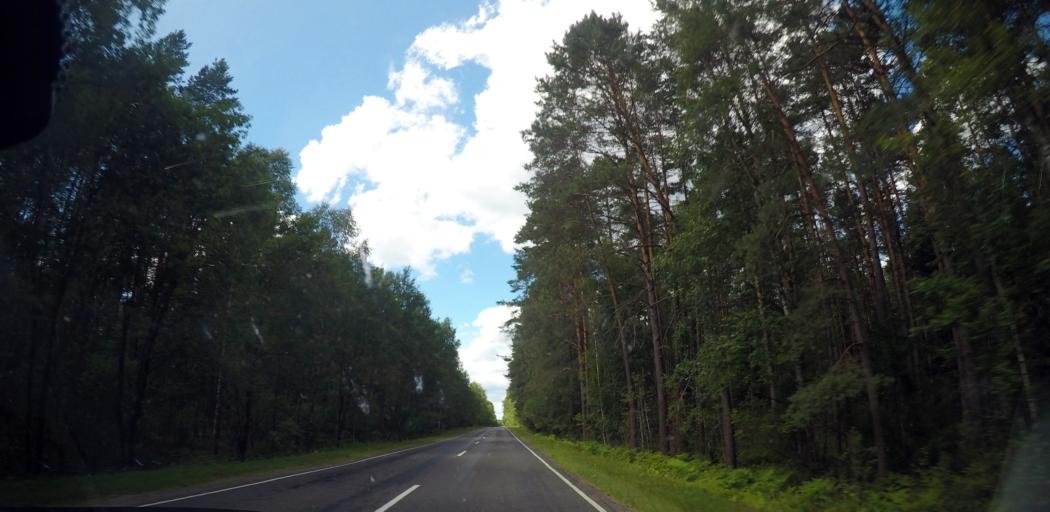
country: BY
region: Grodnenskaya
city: Skidal'
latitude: 53.8435
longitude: 24.2099
